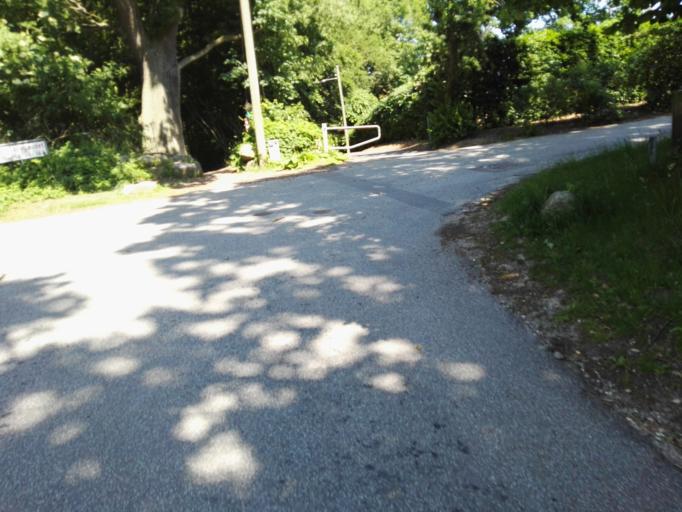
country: DK
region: Capital Region
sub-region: Ballerup Kommune
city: Ballerup
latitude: 55.7531
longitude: 12.3842
